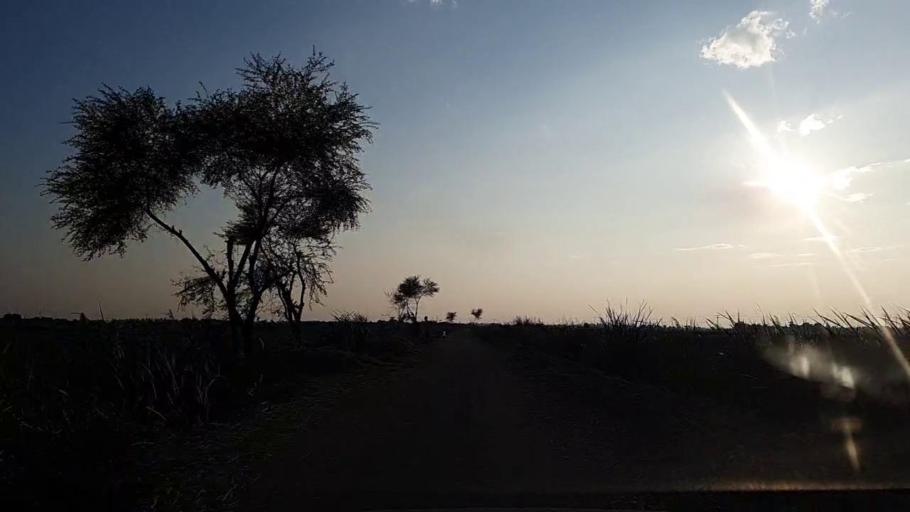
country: PK
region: Sindh
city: Sanghar
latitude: 26.2621
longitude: 68.9789
